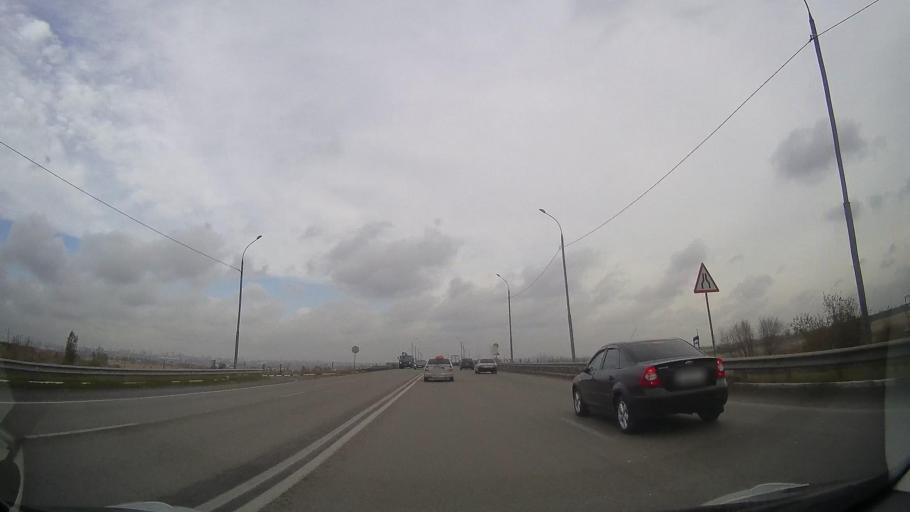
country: RU
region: Rostov
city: Bataysk
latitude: 47.1646
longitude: 39.7423
